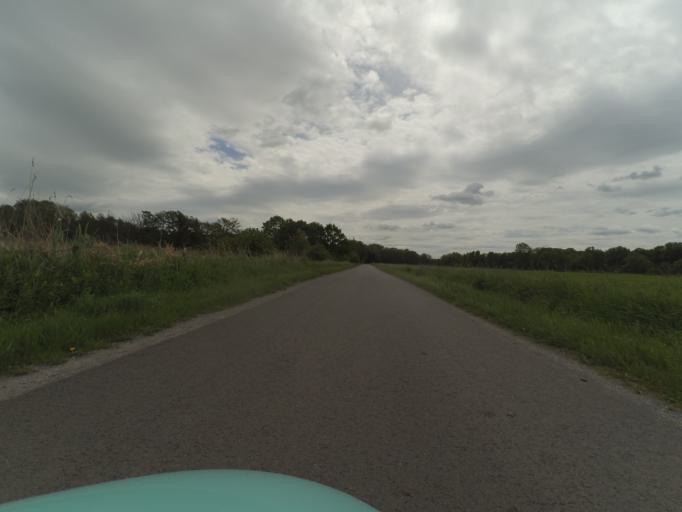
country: DE
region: Lower Saxony
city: Hagenburg
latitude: 52.4401
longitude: 9.3215
